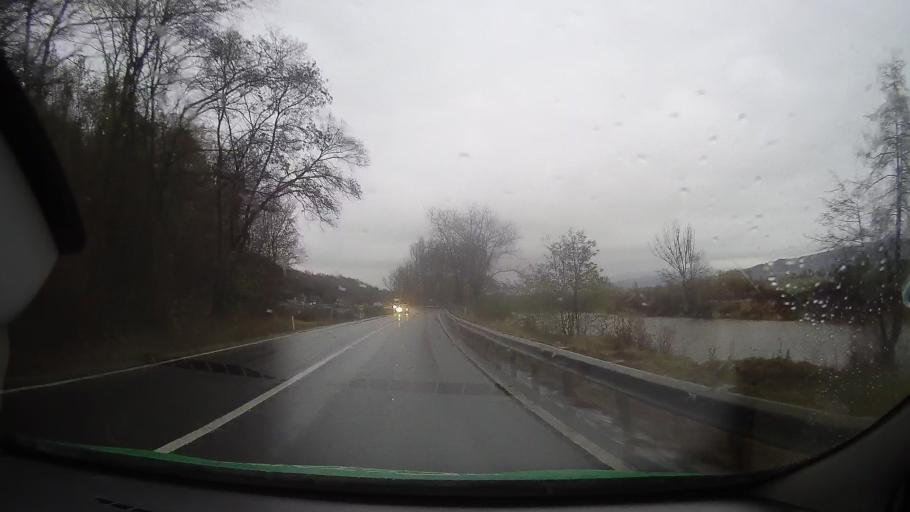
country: RO
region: Mures
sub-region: Comuna Brancovenesti
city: Brancovenesti
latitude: 46.8750
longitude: 24.7748
